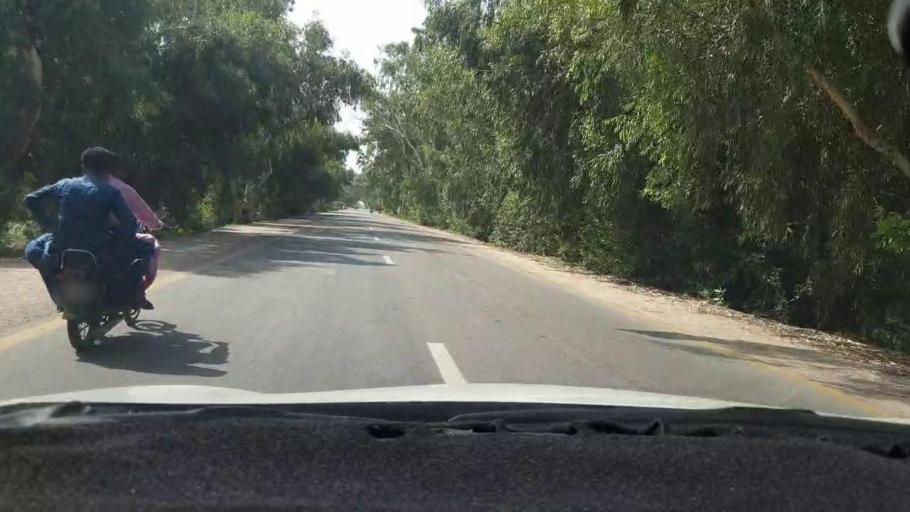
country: PK
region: Sindh
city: Mirpur Khas
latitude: 25.6599
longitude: 69.1006
